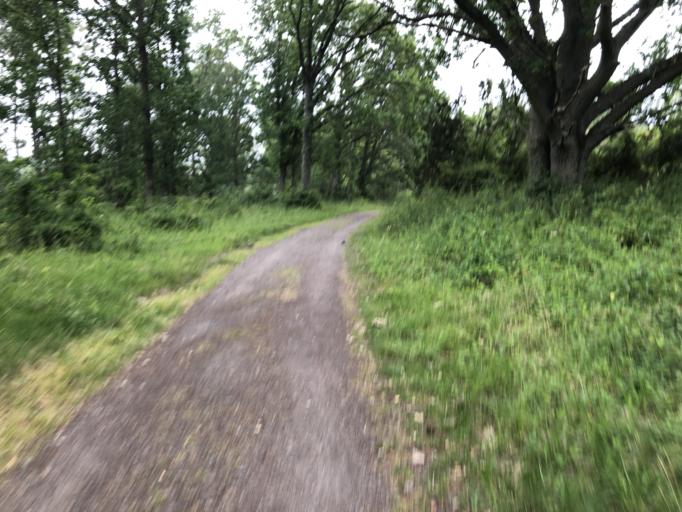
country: SE
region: Kalmar
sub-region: Kalmar Kommun
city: Kalmar
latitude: 56.6353
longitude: 16.3205
